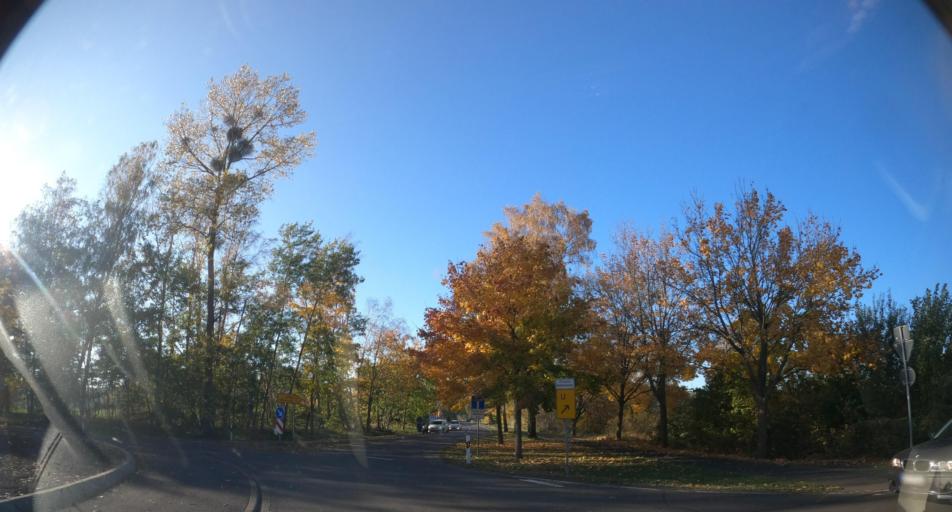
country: DE
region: Mecklenburg-Vorpommern
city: Ueckermunde
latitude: 53.7362
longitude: 14.0931
